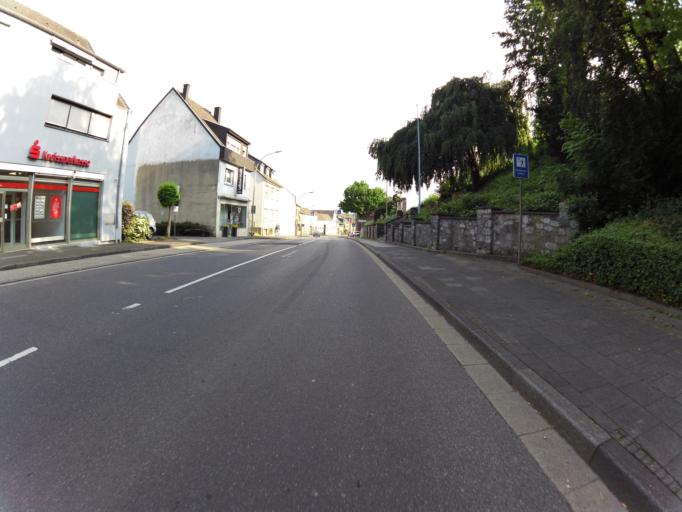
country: DE
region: North Rhine-Westphalia
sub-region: Regierungsbezirk Koln
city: Ubach-Palenberg
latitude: 50.9421
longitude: 6.1058
